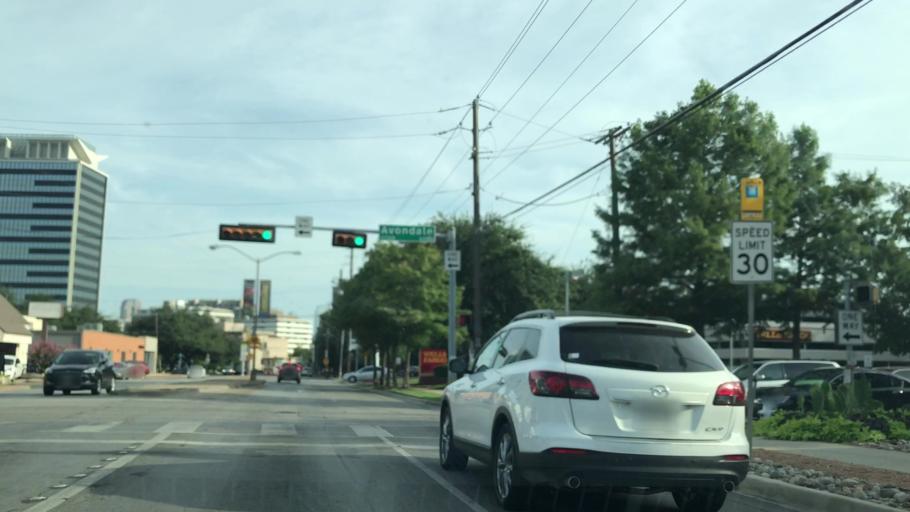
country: US
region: Texas
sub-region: Dallas County
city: Highland Park
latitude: 32.8176
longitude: -96.8024
